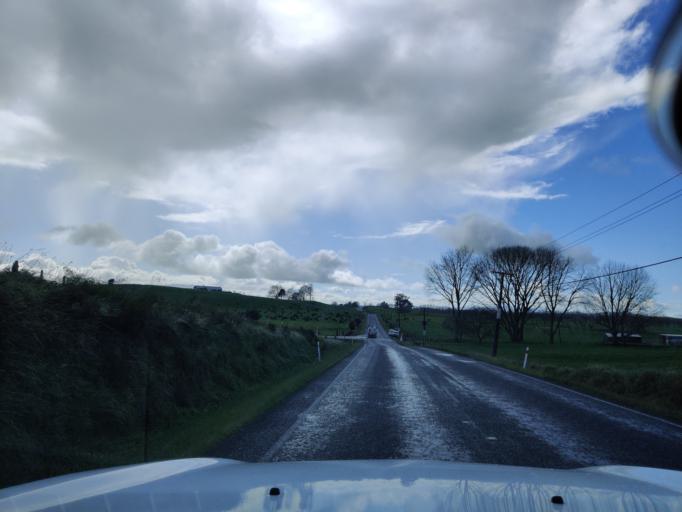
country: NZ
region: Waikato
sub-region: Waikato District
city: Ngaruawahia
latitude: -37.5767
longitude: 175.2342
